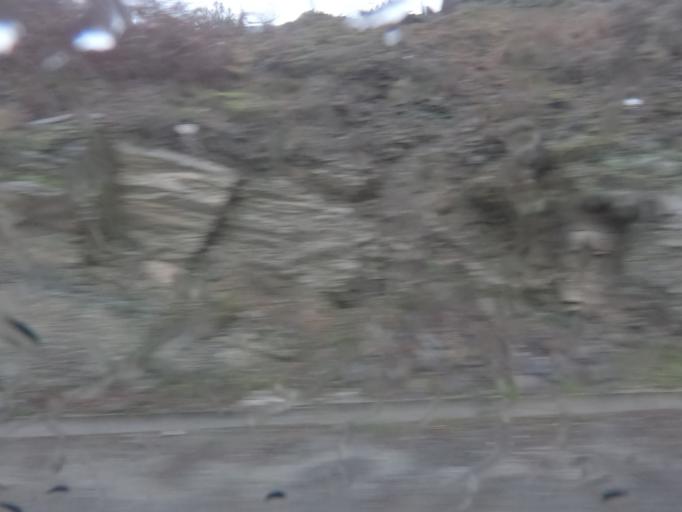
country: PT
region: Vila Real
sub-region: Peso da Regua
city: Peso da Regua
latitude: 41.1680
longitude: -7.7380
